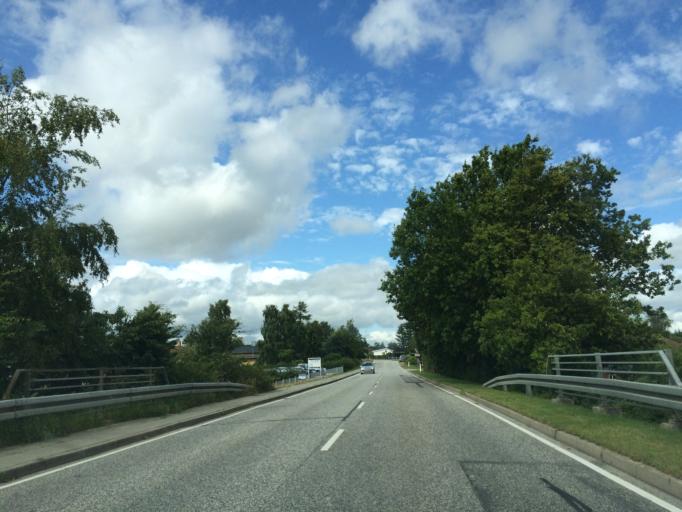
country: DK
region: Central Jutland
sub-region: Silkeborg Kommune
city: Svejbaek
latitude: 56.1905
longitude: 9.6919
